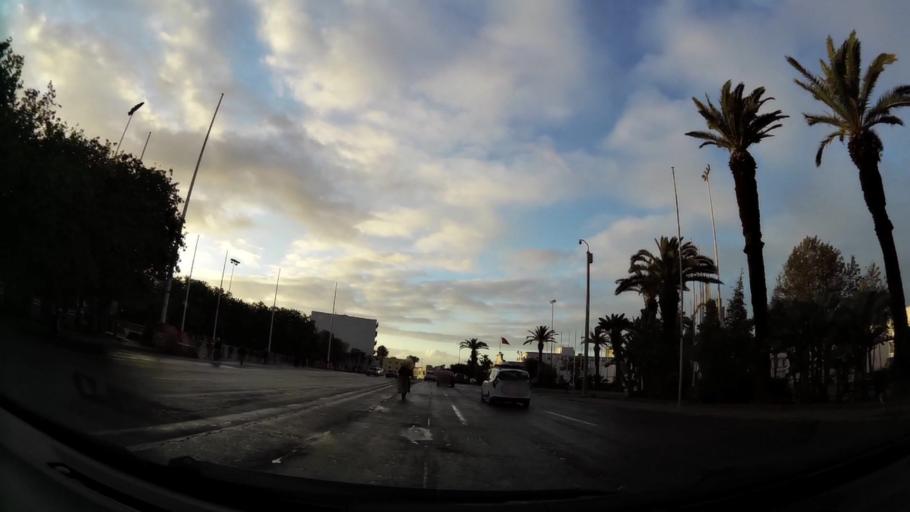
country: MA
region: Grand Casablanca
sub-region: Casablanca
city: Casablanca
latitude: 33.5807
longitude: -7.6017
